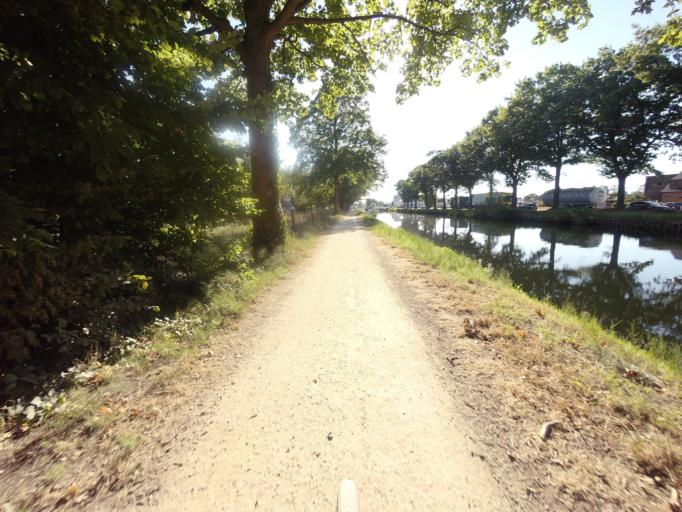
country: BE
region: Flanders
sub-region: Provincie Antwerpen
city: Beerse
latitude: 51.3250
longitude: 4.8350
